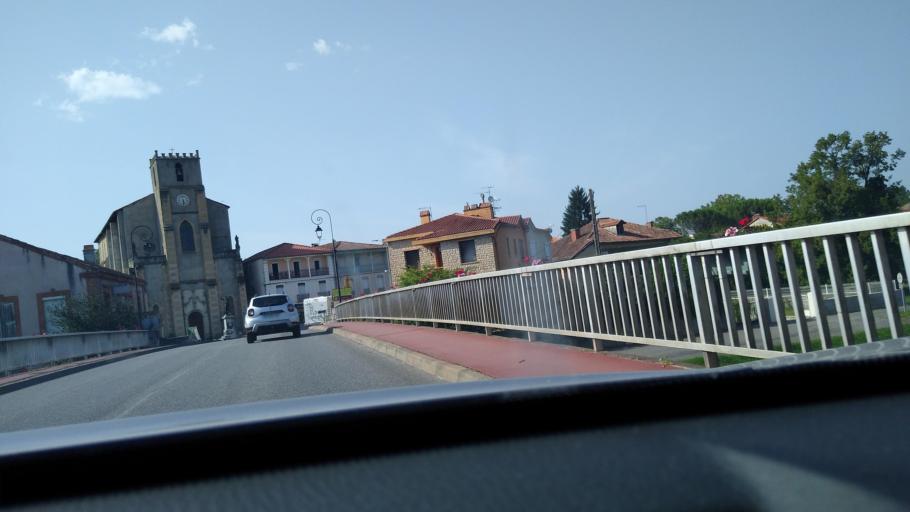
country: FR
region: Midi-Pyrenees
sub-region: Departement de la Haute-Garonne
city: Salies-du-Salat
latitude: 43.0820
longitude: 0.9518
